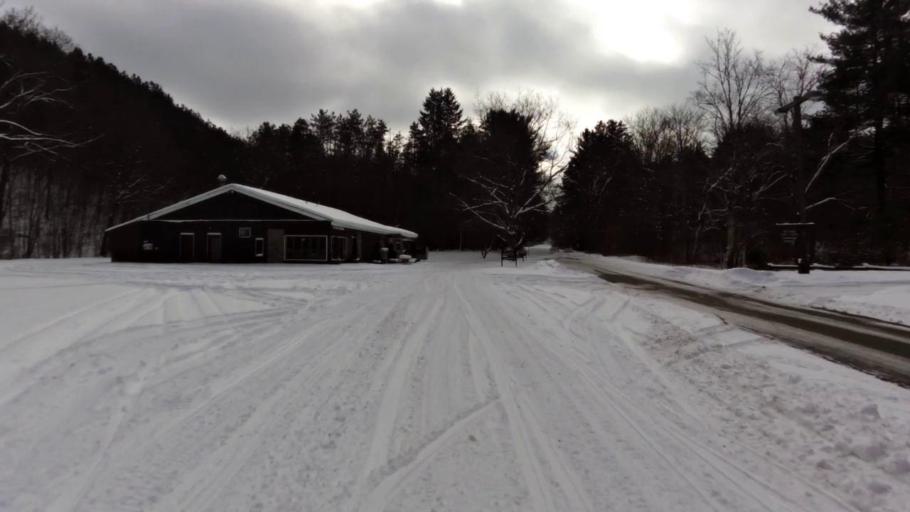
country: US
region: New York
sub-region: Cattaraugus County
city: Salamanca
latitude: 42.0921
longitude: -78.7472
